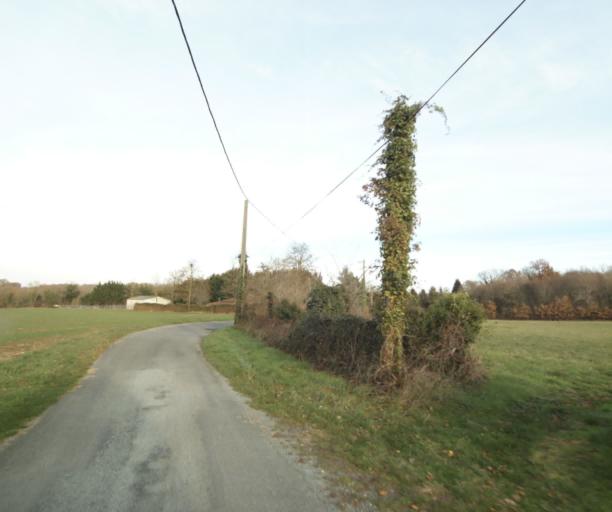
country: FR
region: Poitou-Charentes
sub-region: Departement de la Charente-Maritime
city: Saint-Hilaire-de-Villefranche
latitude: 45.8162
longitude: -0.5616
